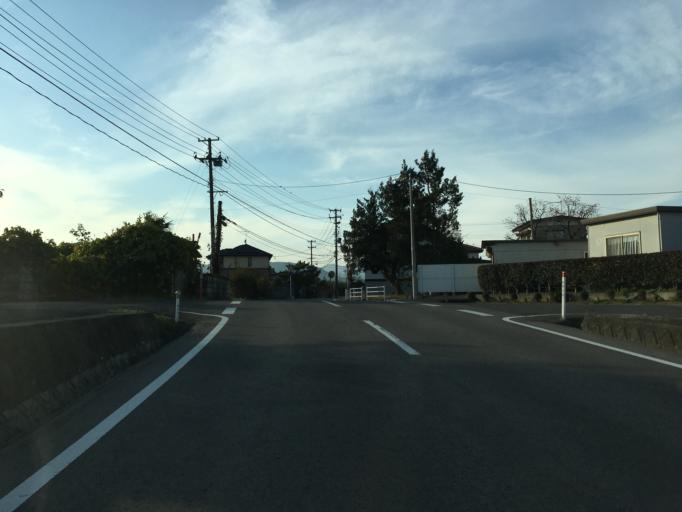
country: JP
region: Fukushima
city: Fukushima-shi
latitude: 37.8060
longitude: 140.4632
